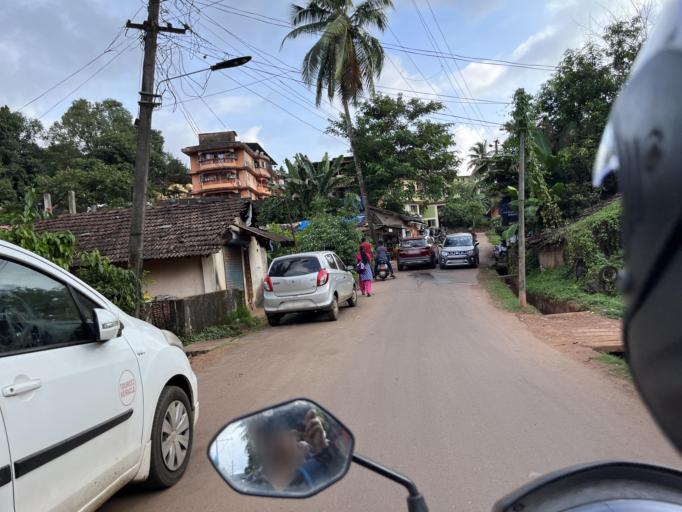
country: IN
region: Goa
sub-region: North Goa
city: Ponda
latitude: 15.4075
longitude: 74.0121
